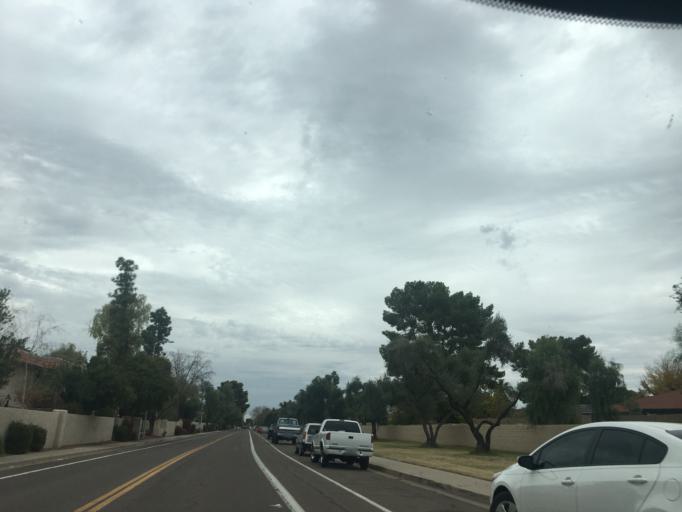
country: US
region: Arizona
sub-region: Maricopa County
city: Guadalupe
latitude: 33.3712
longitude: -111.9241
